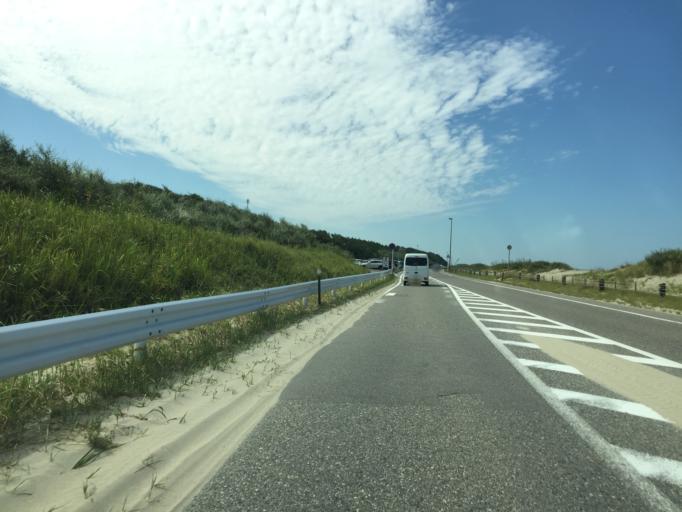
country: JP
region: Niigata
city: Niigata-shi
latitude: 37.9389
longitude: 139.0524
